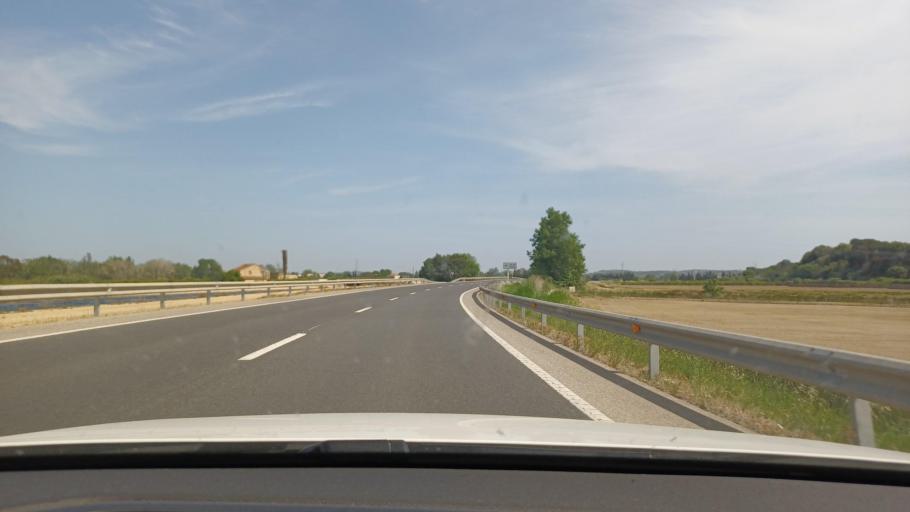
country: ES
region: Catalonia
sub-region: Provincia de Tarragona
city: Tortosa
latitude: 40.7746
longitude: 0.5262
